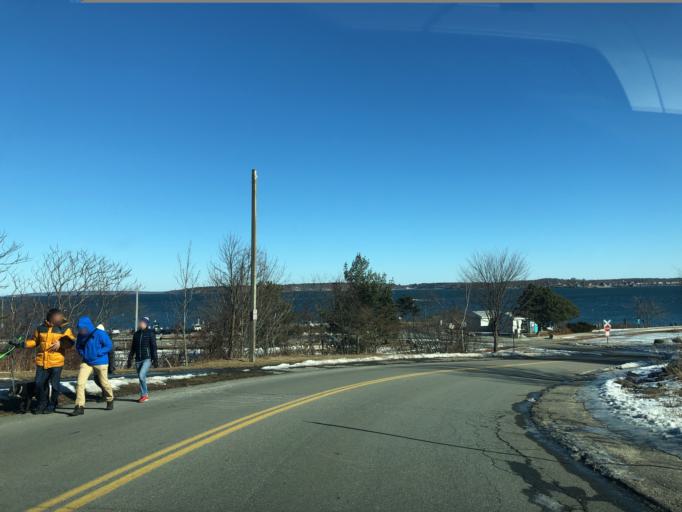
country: US
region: Maine
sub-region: Cumberland County
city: Portland
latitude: 43.6696
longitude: -70.2428
